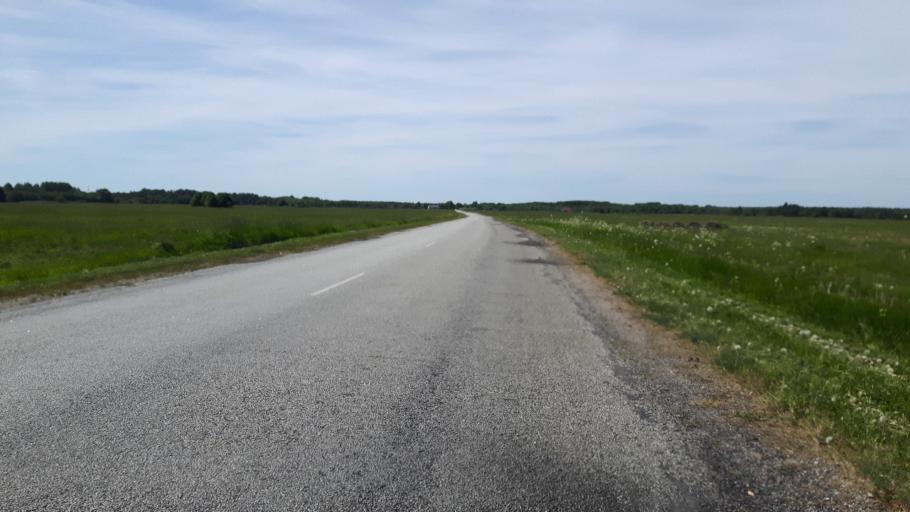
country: EE
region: Harju
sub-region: Kuusalu vald
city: Kuusalu
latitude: 59.4623
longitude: 25.3351
